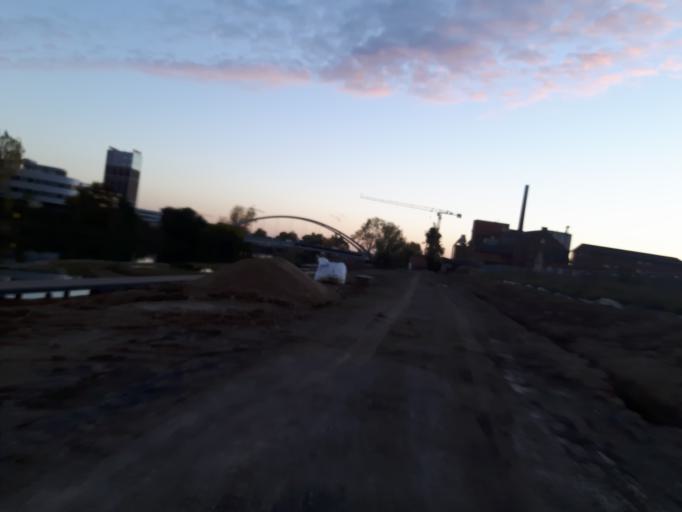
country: DE
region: Baden-Wuerttemberg
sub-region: Regierungsbezirk Stuttgart
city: Heilbronn
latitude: 49.1545
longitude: 9.2101
